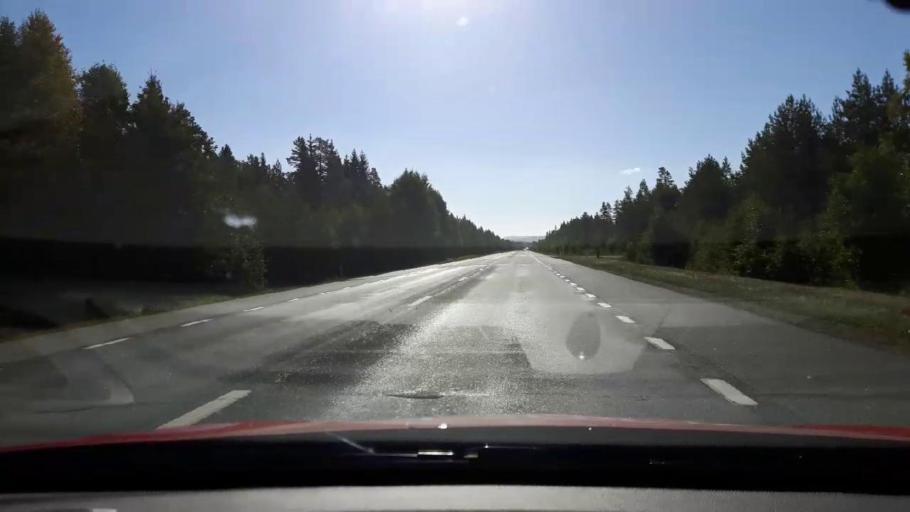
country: SE
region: Vaesternorrland
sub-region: Ange Kommun
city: Ange
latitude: 62.5922
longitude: 15.7117
